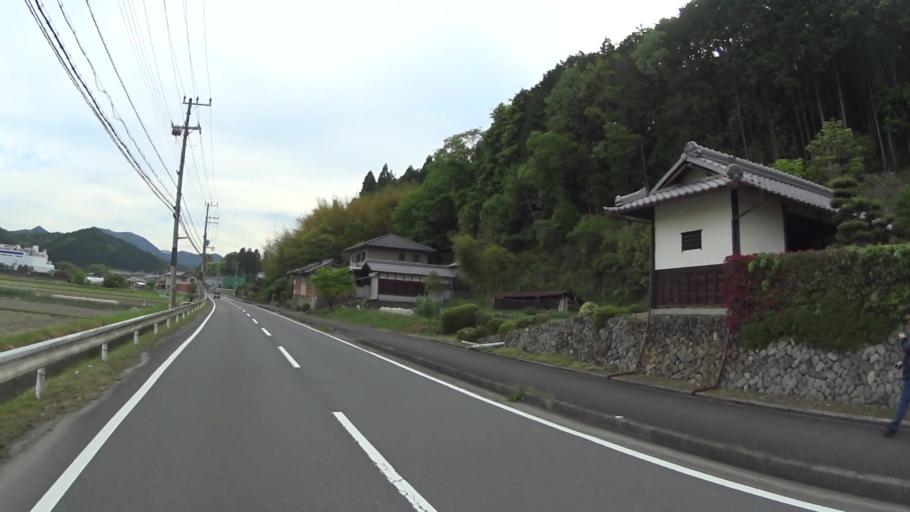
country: JP
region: Kyoto
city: Kameoka
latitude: 35.0997
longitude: 135.5098
